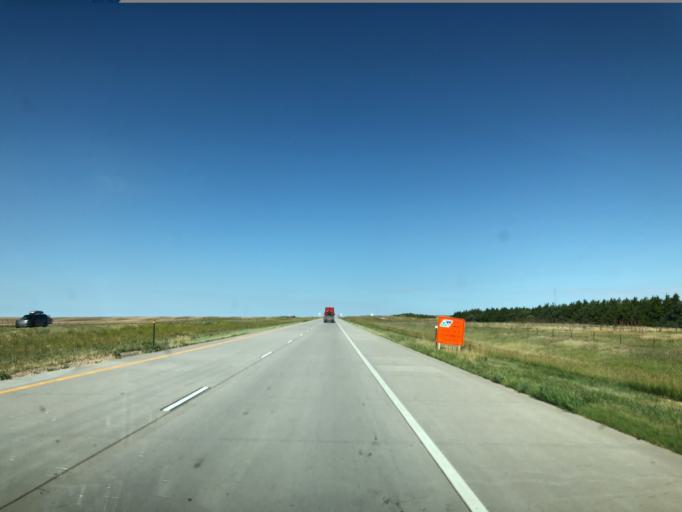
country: US
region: Colorado
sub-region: Kit Carson County
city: Burlington
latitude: 39.2940
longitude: -102.8414
